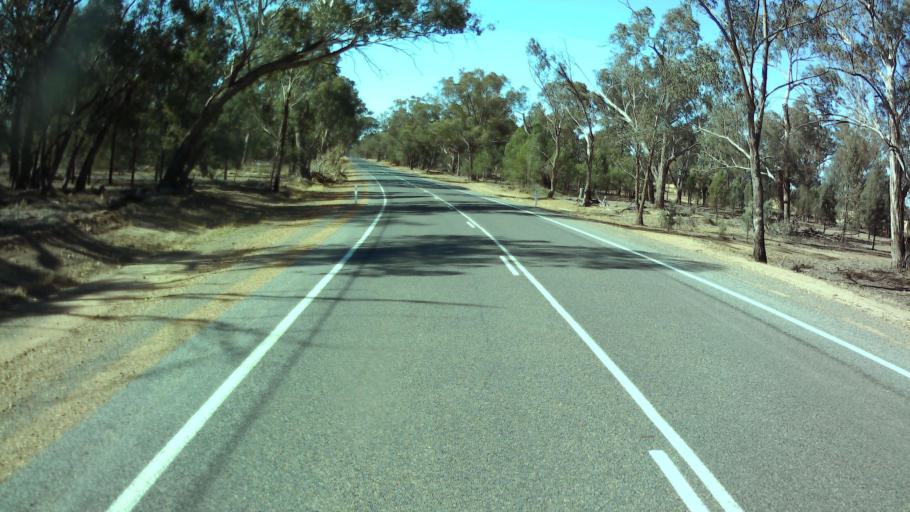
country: AU
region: New South Wales
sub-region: Weddin
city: Grenfell
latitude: -33.7442
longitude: 148.0885
